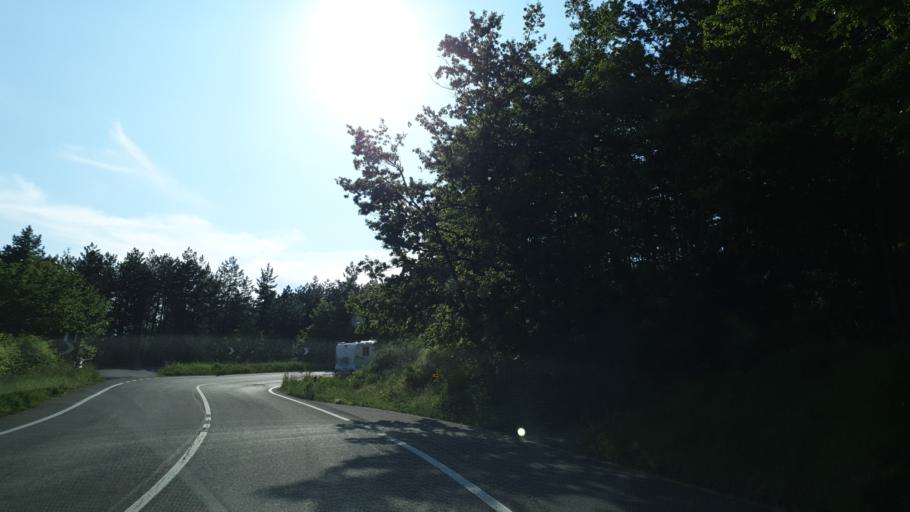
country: IT
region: Tuscany
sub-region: Province of Arezzo
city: Stia
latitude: 43.7798
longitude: 11.6742
